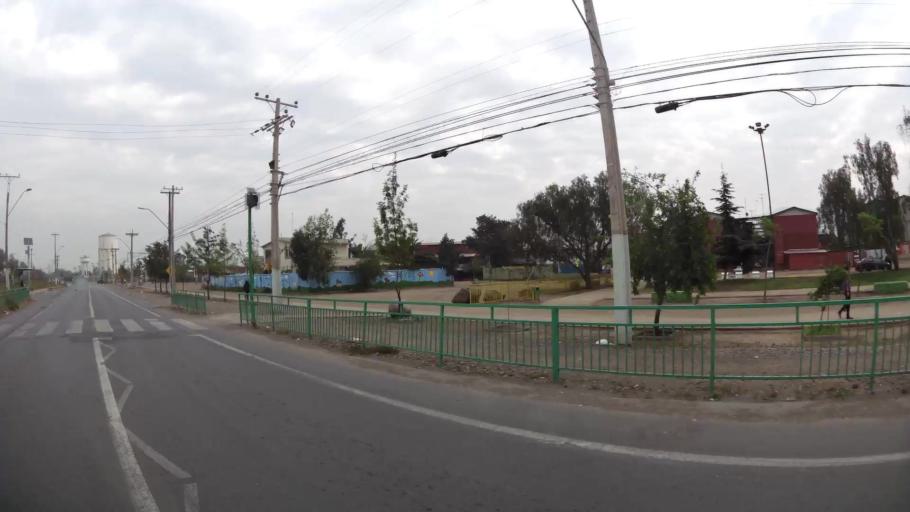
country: CL
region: Santiago Metropolitan
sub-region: Provincia de Chacabuco
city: Chicureo Abajo
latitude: -33.1962
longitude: -70.6688
